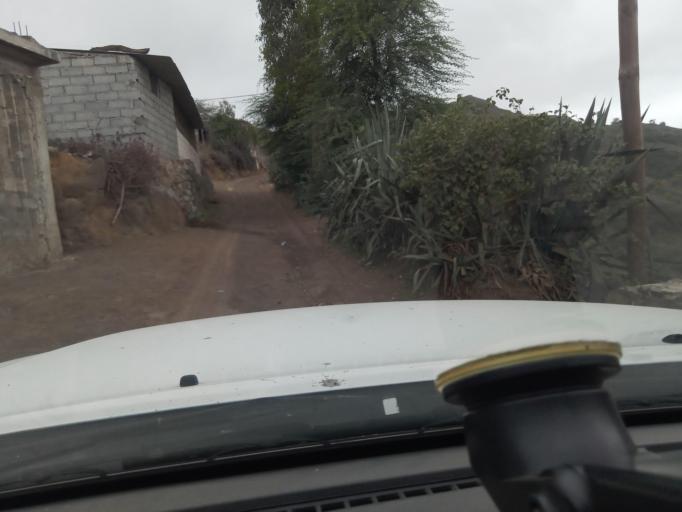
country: CV
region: Santa Catarina
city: Assomada
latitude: 15.1385
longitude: -23.6451
